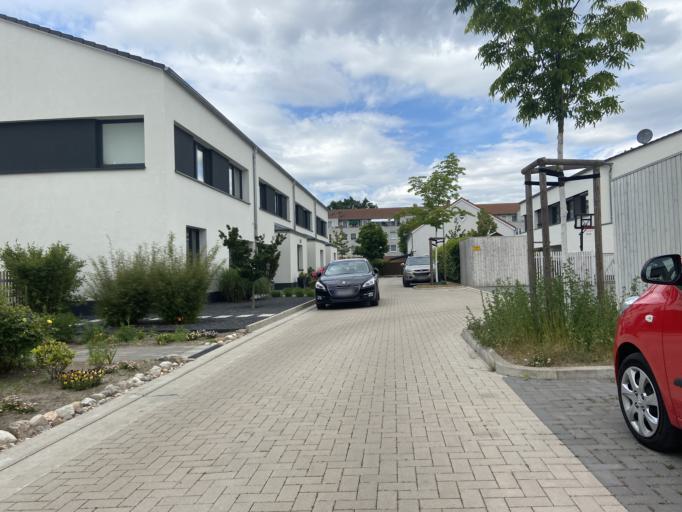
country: DE
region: Lower Saxony
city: Isernhagen Farster Bauerschaft
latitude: 52.3918
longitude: 9.8359
